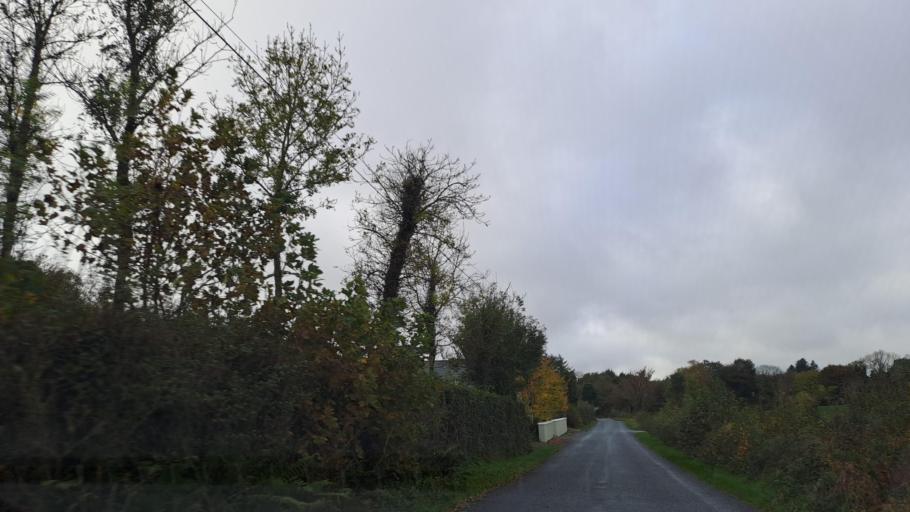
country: IE
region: Ulster
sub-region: An Cabhan
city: Bailieborough
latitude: 53.9923
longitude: -6.9846
